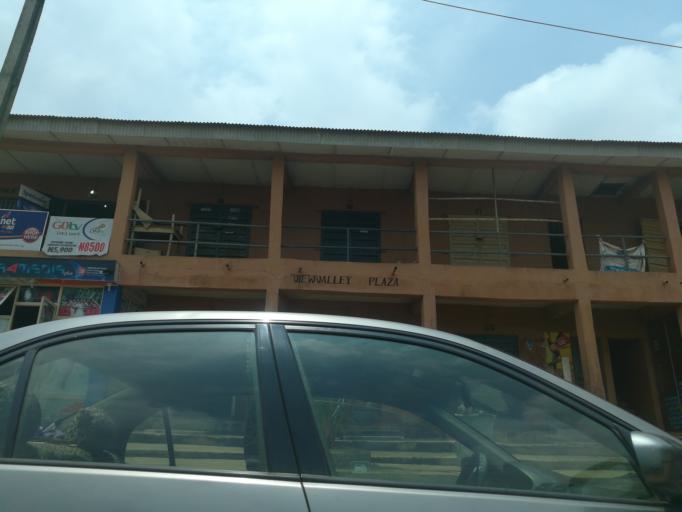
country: NG
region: Lagos
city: Ikorodu
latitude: 6.6282
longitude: 3.5312
